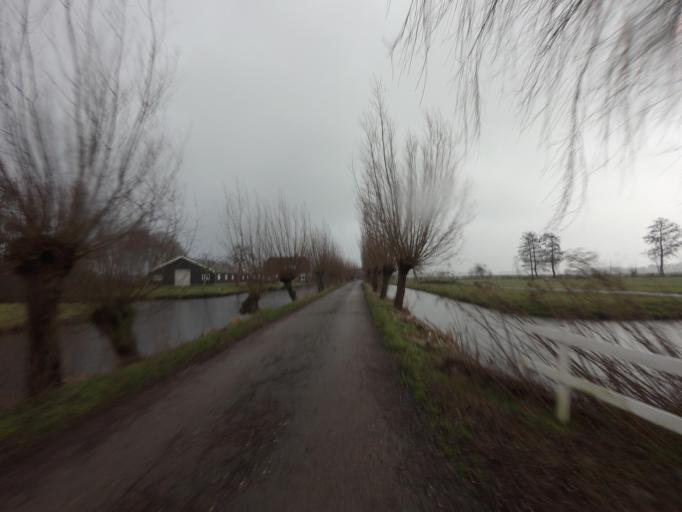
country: NL
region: Utrecht
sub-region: Gemeente Montfoort
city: Montfoort
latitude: 52.0784
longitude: 4.9485
